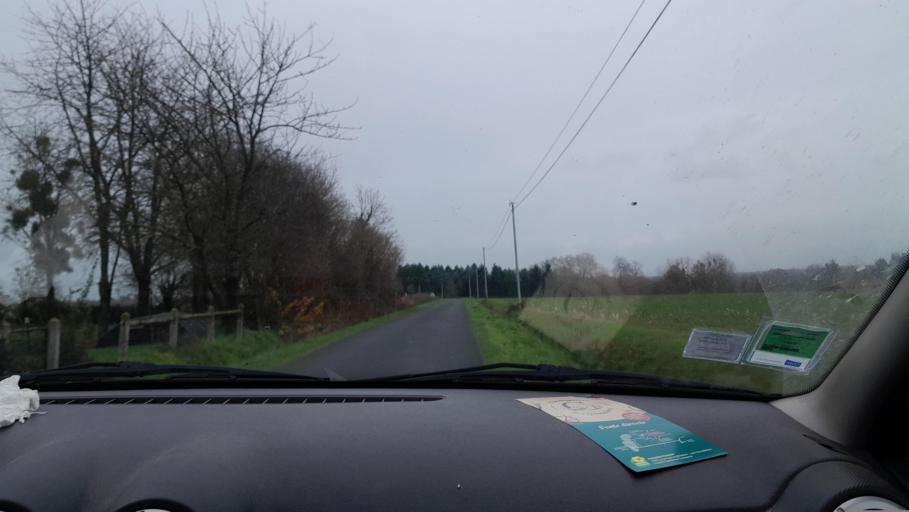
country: FR
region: Brittany
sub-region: Departement d'Ille-et-Vilaine
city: La Guerche-de-Bretagne
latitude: 47.9148
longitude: -1.1545
